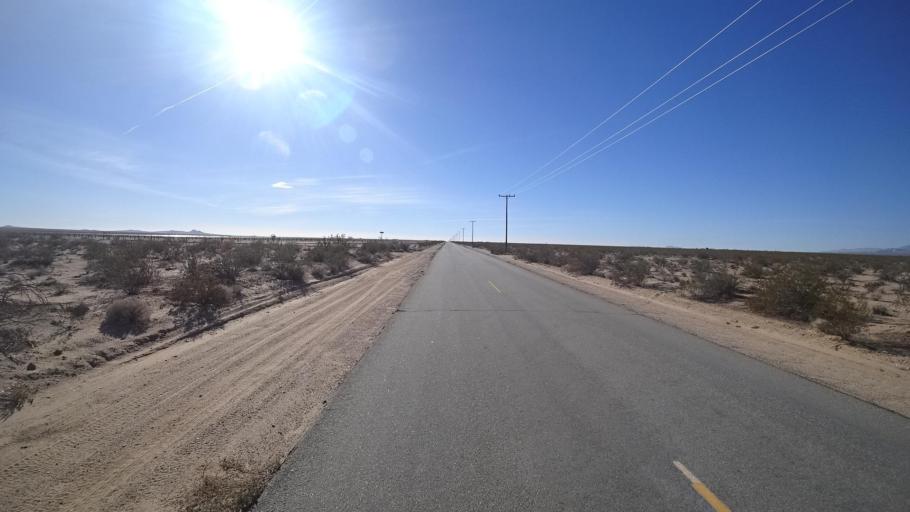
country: US
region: California
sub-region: Kern County
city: California City
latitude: 35.2283
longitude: -117.9859
